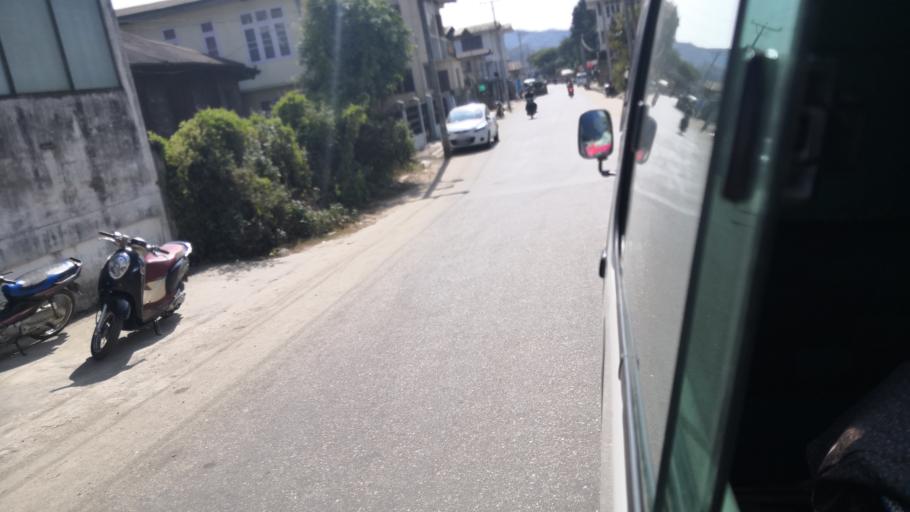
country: MM
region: Mandalay
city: Mogok
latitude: 22.9265
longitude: 96.5049
